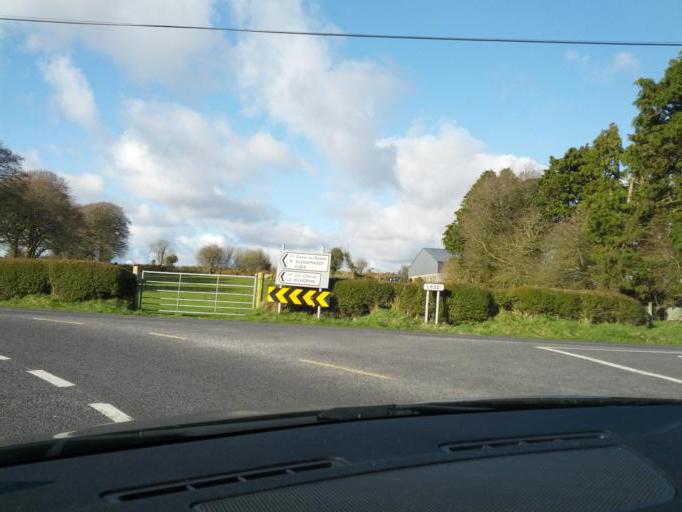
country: IE
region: Connaught
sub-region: Roscommon
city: Castlerea
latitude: 53.5446
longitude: -8.5517
